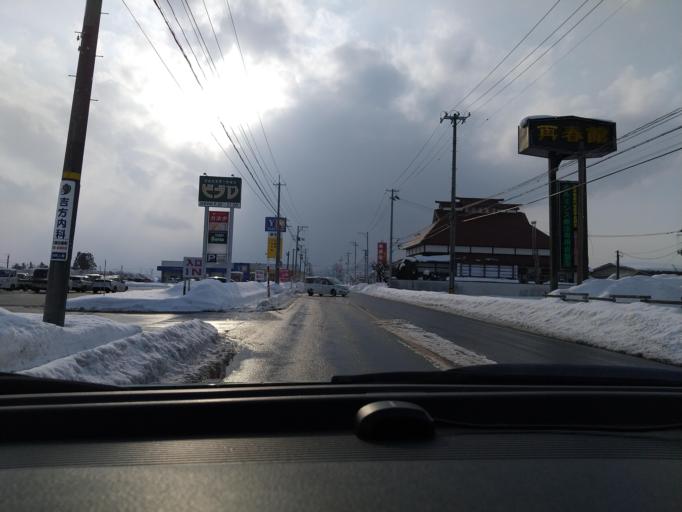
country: JP
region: Akita
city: Omagari
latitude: 39.4887
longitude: 140.4952
